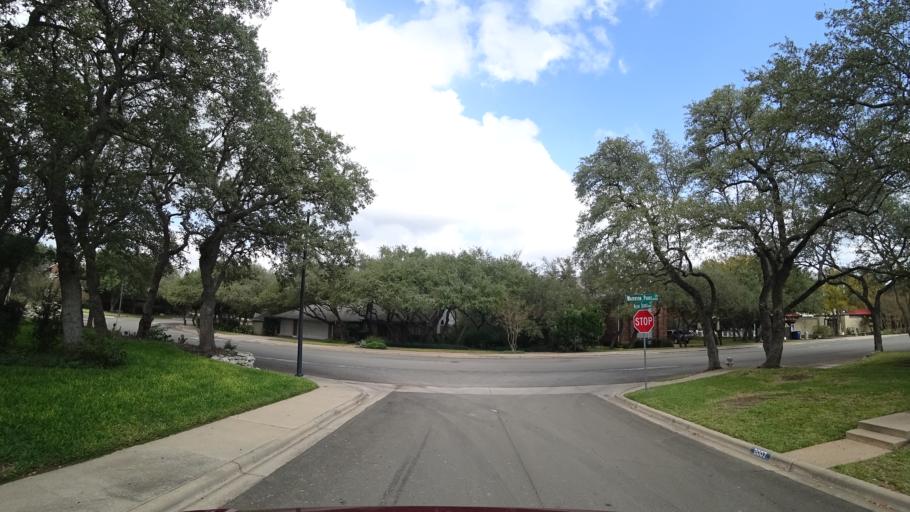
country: US
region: Texas
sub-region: Williamson County
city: Anderson Mill
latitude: 30.4198
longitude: -97.8601
